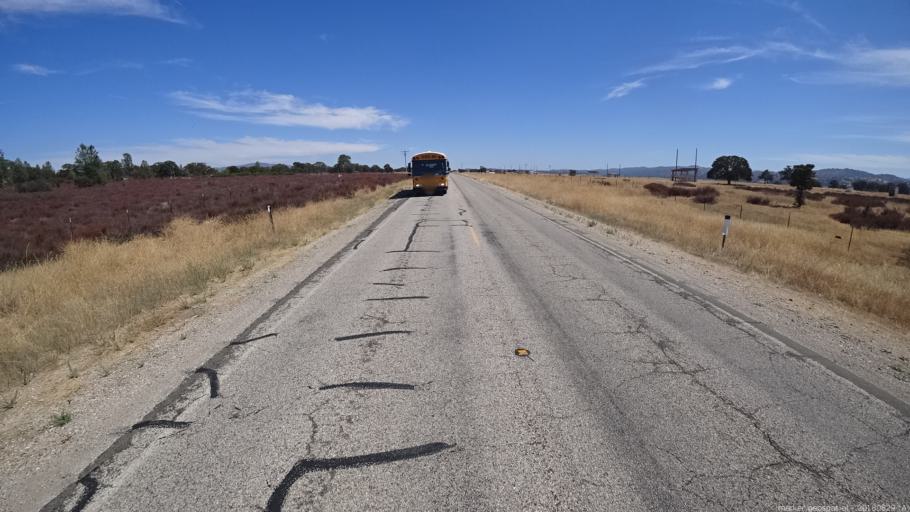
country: US
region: California
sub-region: Monterey County
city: King City
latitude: 35.9645
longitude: -121.1695
